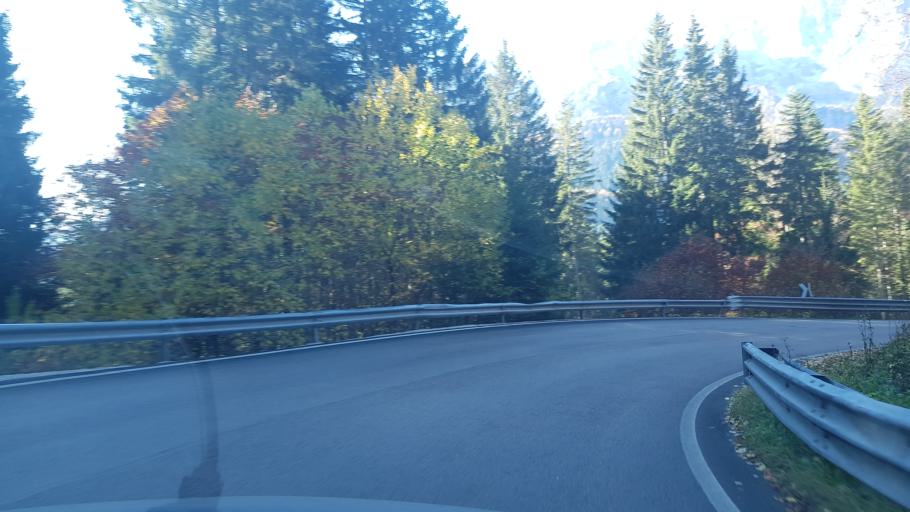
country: IT
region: Veneto
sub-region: Provincia di Belluno
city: Candide
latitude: 46.6323
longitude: 12.4646
